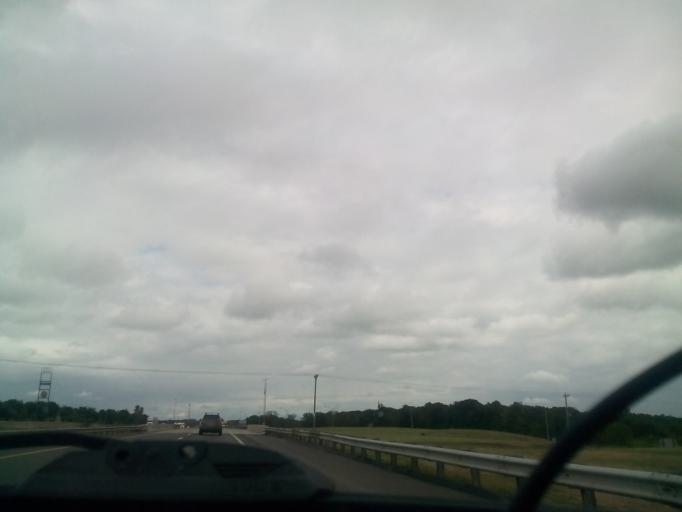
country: US
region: Ohio
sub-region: Williams County
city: Montpelier
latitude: 41.6297
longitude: -84.7673
